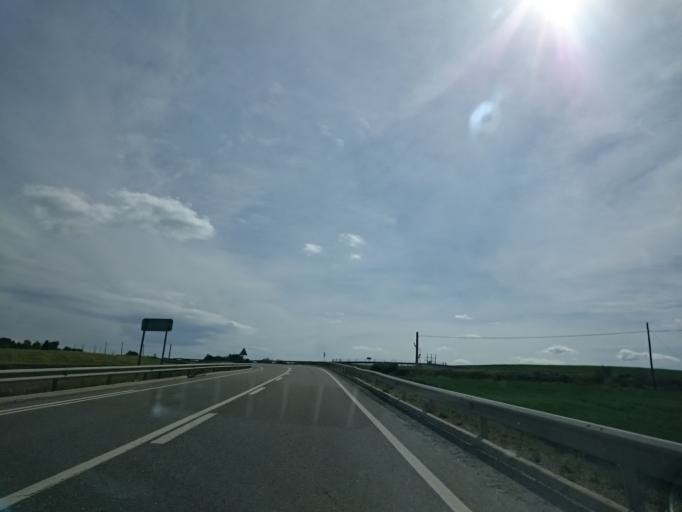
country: ES
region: Catalonia
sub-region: Provincia de Lleida
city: Sant Guim de Freixenet
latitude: 41.6136
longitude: 1.4005
